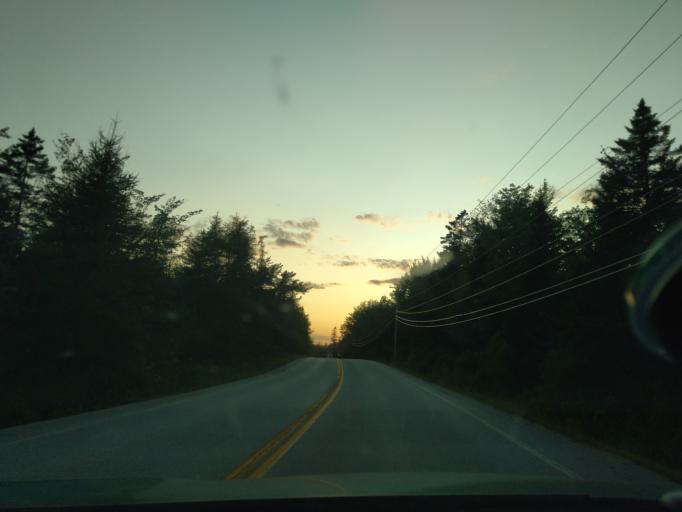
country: US
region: Maine
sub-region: Hancock County
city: Gouldsboro
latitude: 44.3927
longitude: -68.0577
